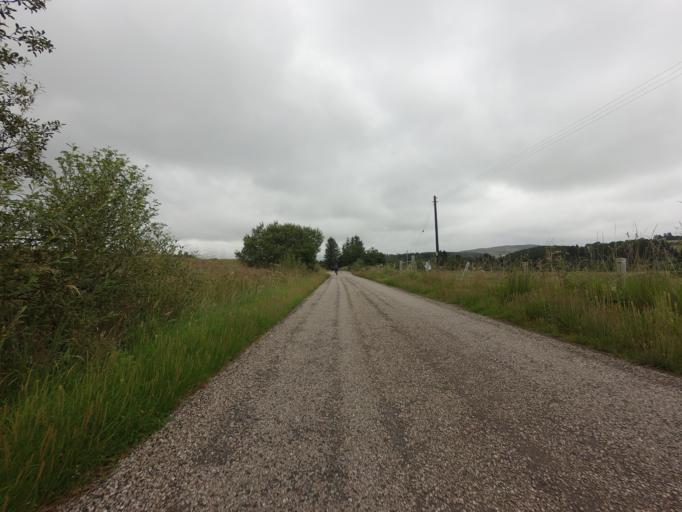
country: GB
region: Scotland
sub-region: Highland
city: Alness
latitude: 58.0073
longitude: -4.4045
